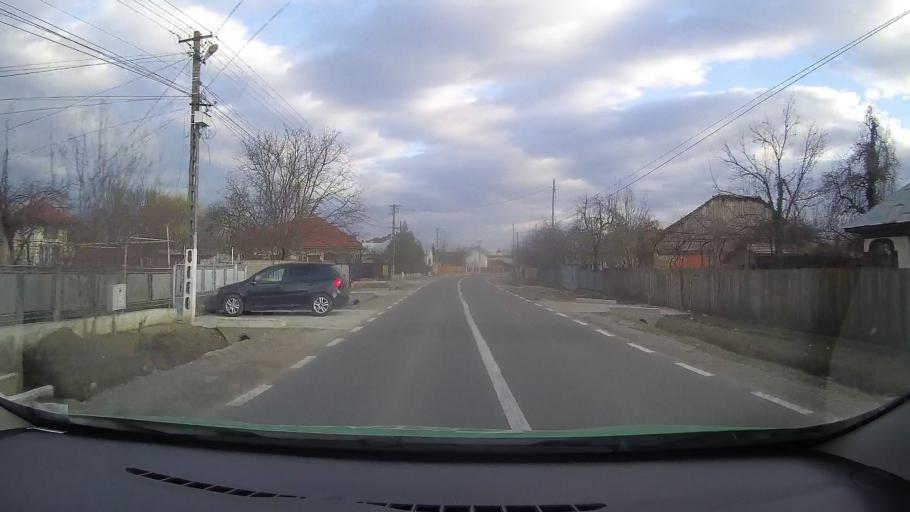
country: RO
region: Dambovita
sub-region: Comuna I. L. Caragiale
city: Ghirdoveni
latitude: 44.9370
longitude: 25.6821
